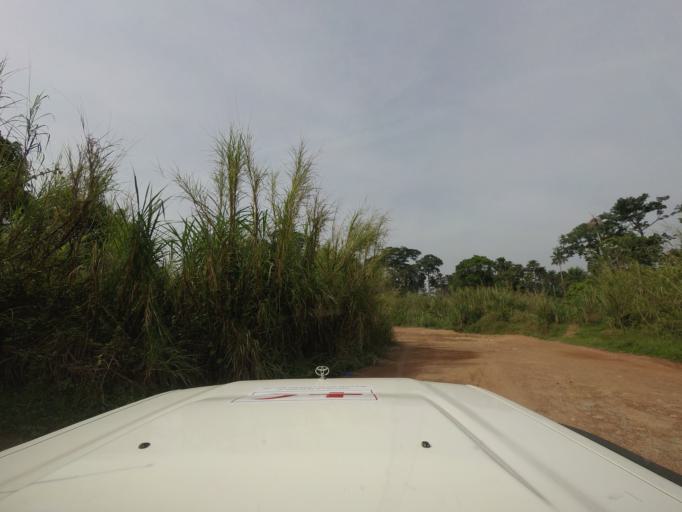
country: GN
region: Nzerekore
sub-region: Macenta
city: Macenta
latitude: 8.5285
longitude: -9.5068
